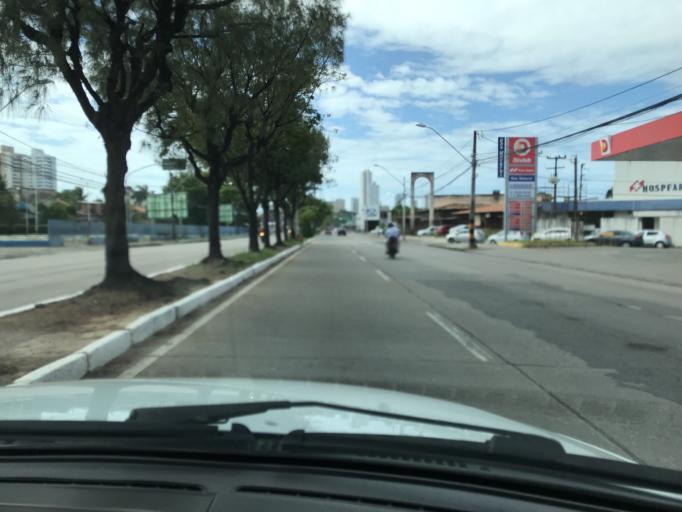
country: BR
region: Pernambuco
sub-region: Recife
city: Recife
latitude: -8.0625
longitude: -34.9162
